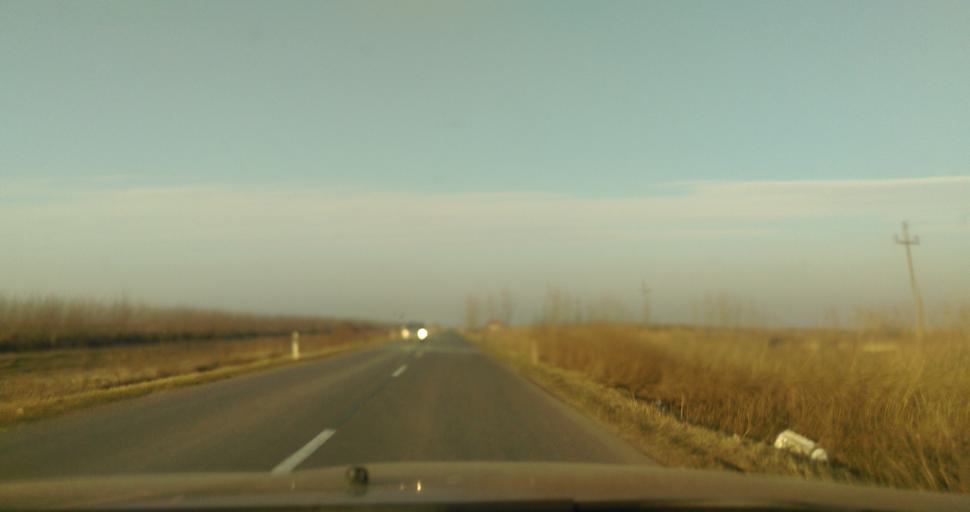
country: RS
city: Curug
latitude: 45.4823
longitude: 20.0402
